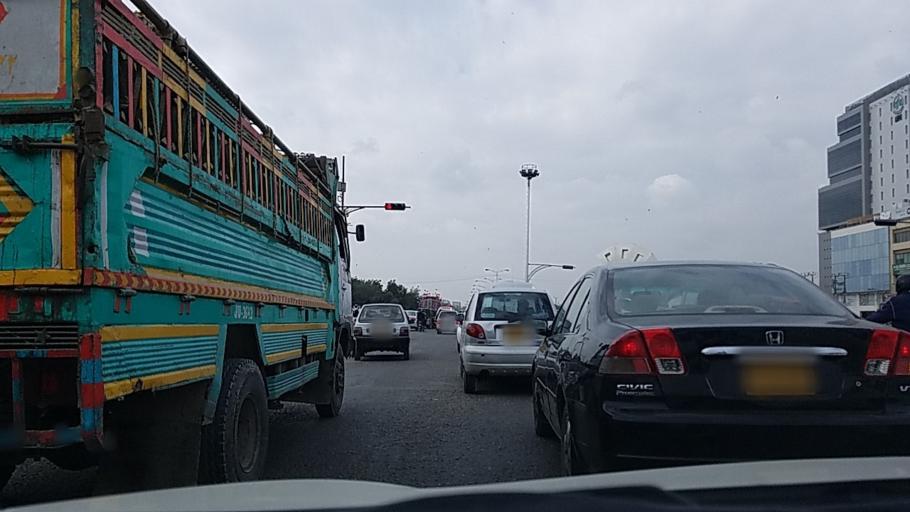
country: PK
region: Sindh
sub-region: Karachi District
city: Karachi
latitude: 24.8366
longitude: 67.0683
